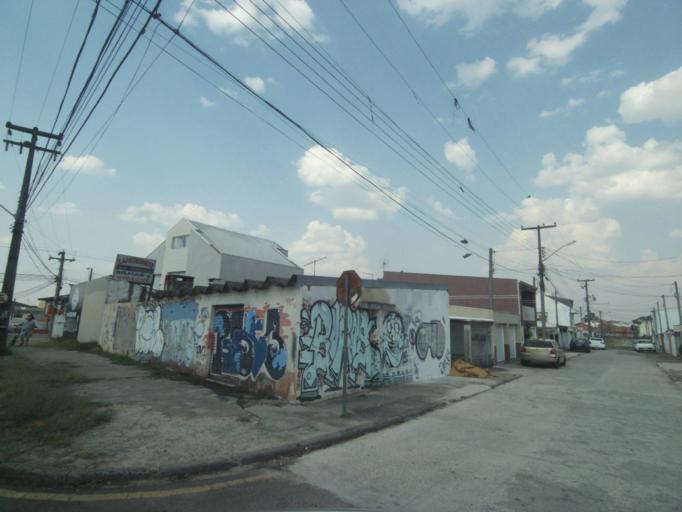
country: BR
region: Parana
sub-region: Sao Jose Dos Pinhais
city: Sao Jose dos Pinhais
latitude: -25.5322
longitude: -49.2424
